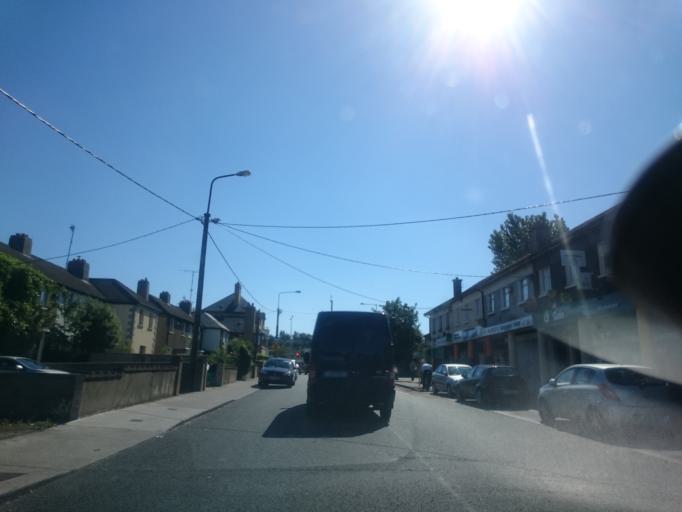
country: IE
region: Leinster
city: Sallynoggin
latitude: 53.2837
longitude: -6.1478
